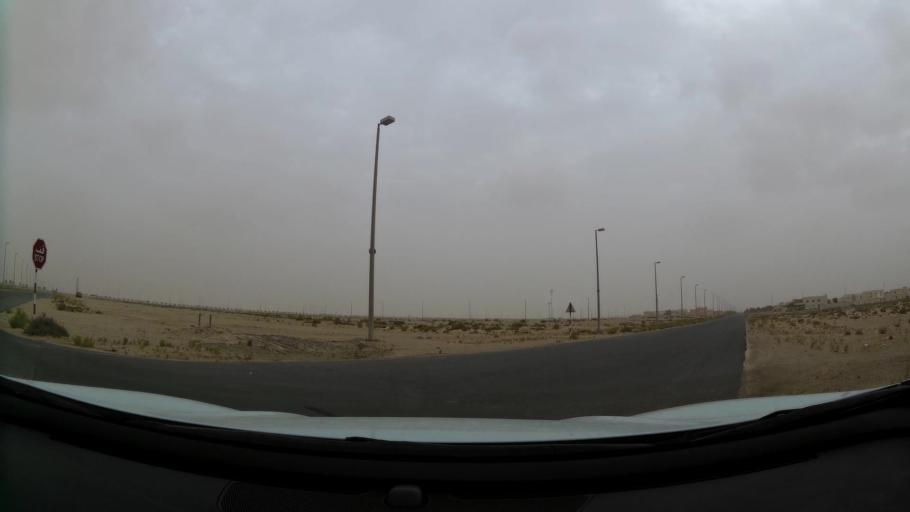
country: AE
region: Abu Dhabi
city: Abu Dhabi
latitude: 24.4181
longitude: 54.6969
